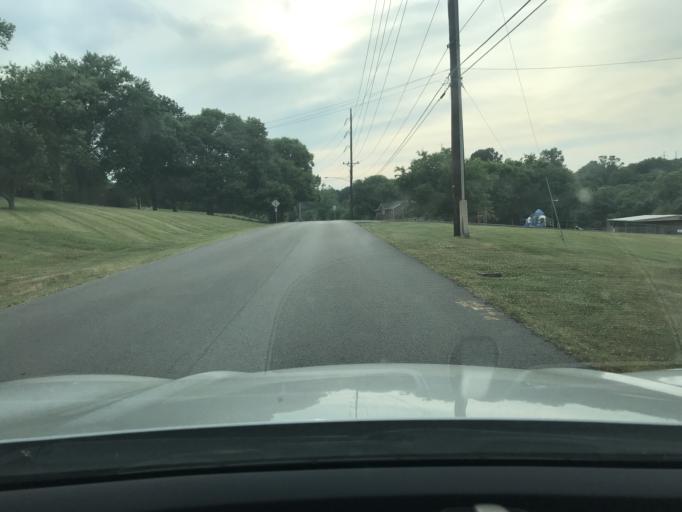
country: US
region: Tennessee
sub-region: Davidson County
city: Goodlettsville
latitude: 36.3135
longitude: -86.7157
